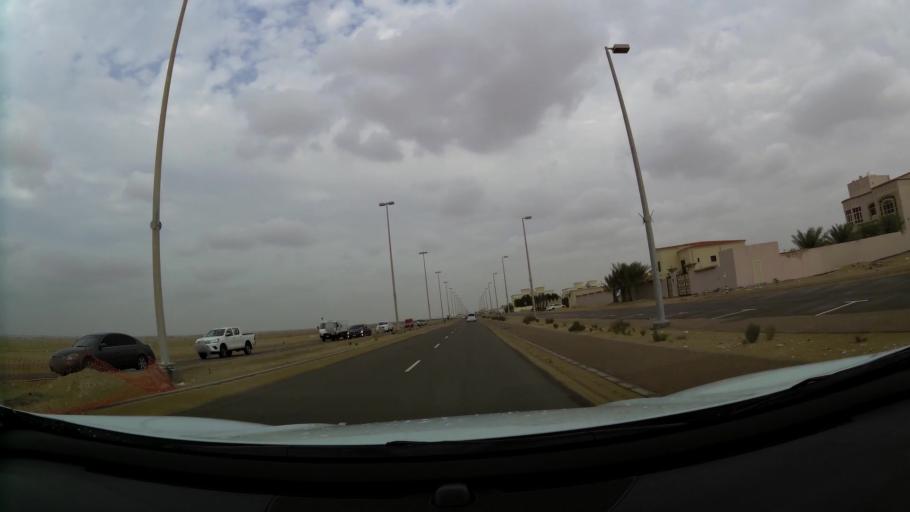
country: AE
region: Abu Dhabi
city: Abu Dhabi
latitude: 24.3593
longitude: 54.6152
